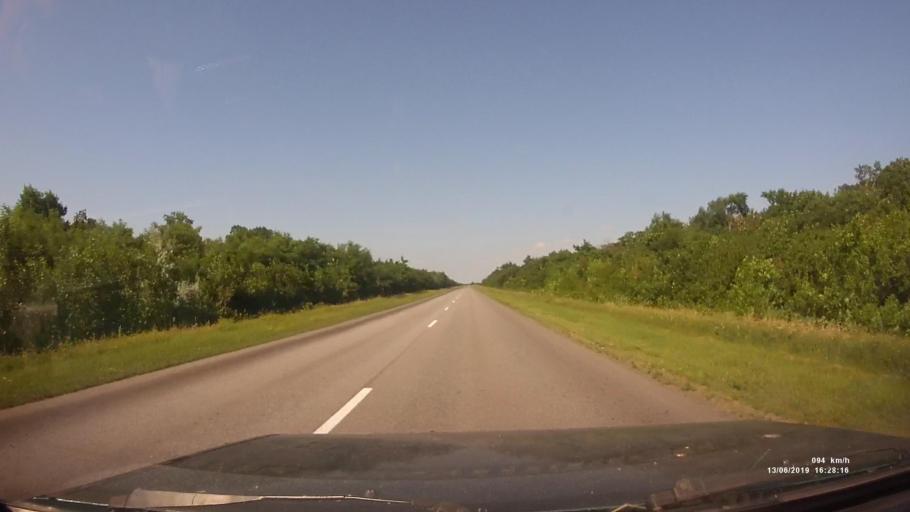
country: RU
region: Rostov
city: Kazanskaya
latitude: 49.8202
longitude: 41.1970
